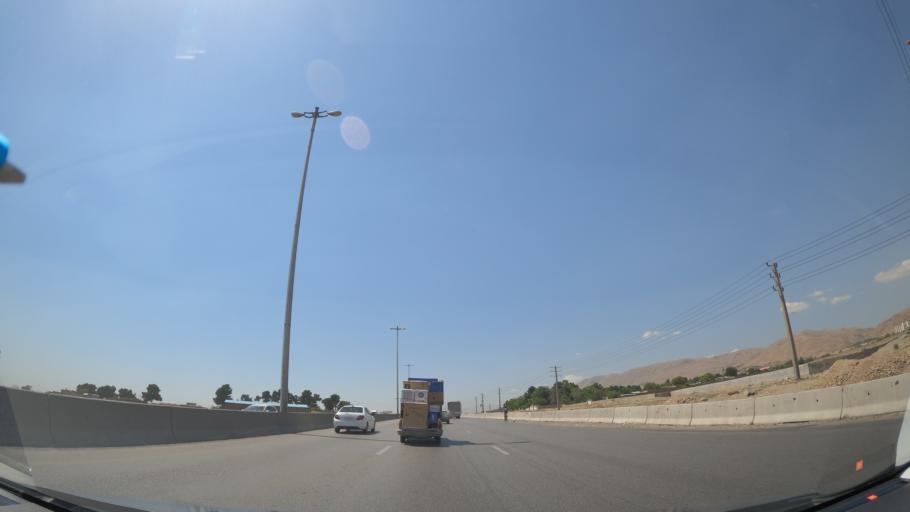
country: IR
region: Alborz
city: Karaj
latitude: 35.8714
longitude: 50.8969
